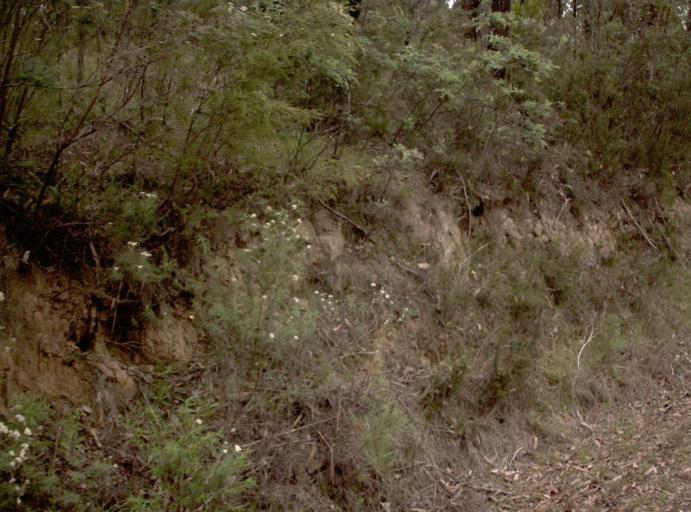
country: AU
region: Victoria
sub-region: East Gippsland
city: Bairnsdale
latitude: -37.6141
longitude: 147.1897
